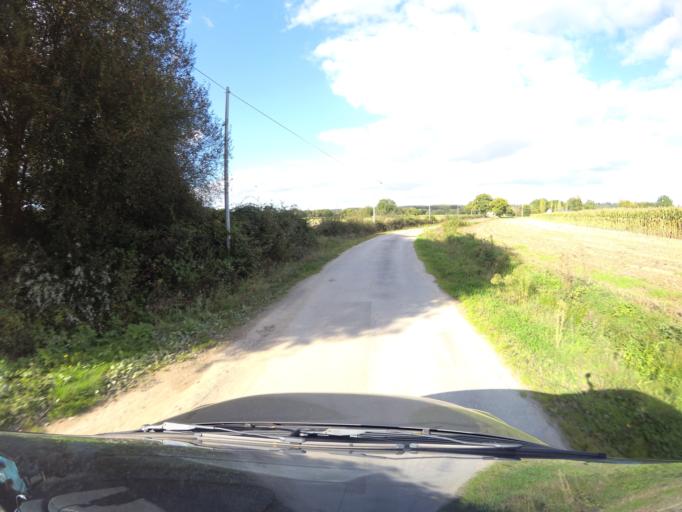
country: FR
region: Brittany
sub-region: Departement du Morbihan
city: Saint-Martin-sur-Oust
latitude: 47.7333
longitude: -2.2434
